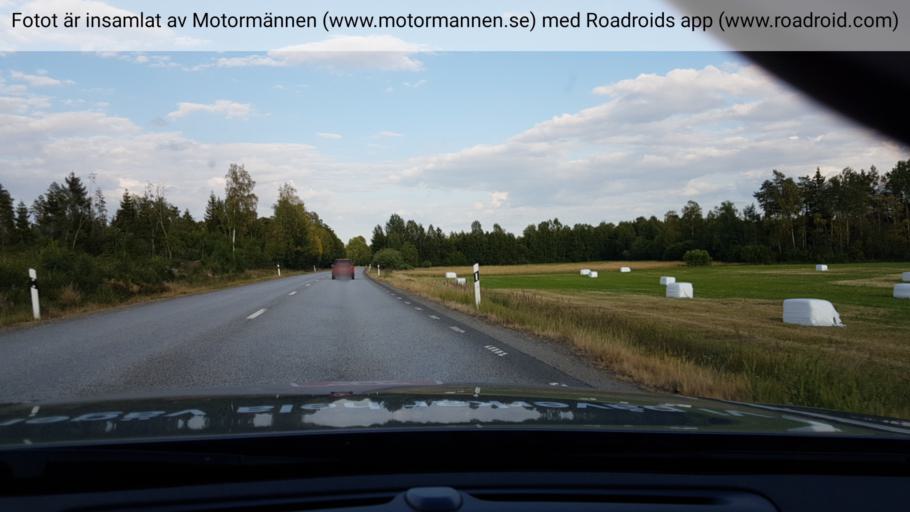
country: SE
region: Uppsala
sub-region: Enkopings Kommun
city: Orsundsbro
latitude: 59.8909
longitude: 17.1673
